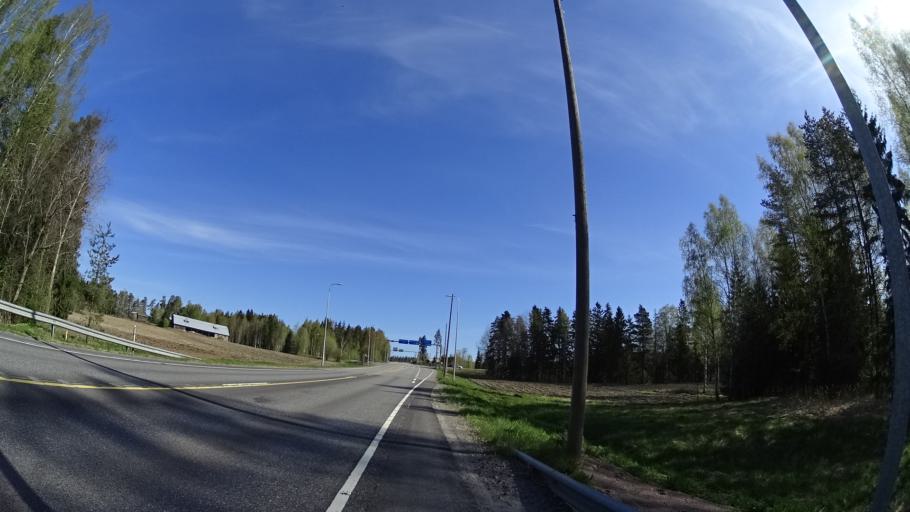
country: FI
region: Uusimaa
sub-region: Helsinki
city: Nurmijaervi
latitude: 60.4358
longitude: 24.8298
